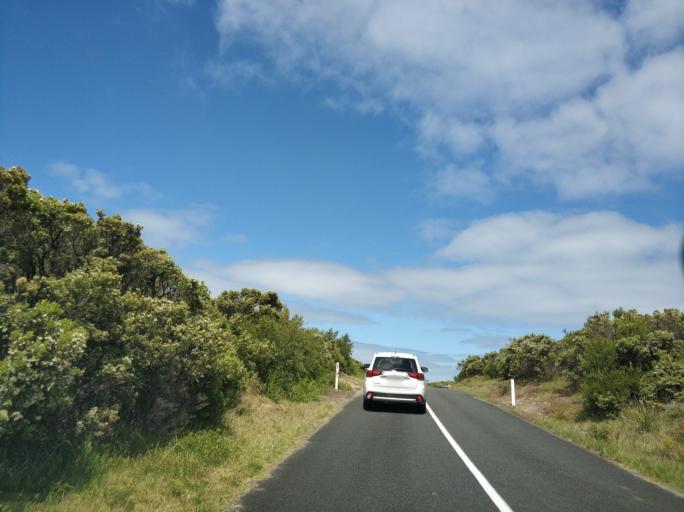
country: AU
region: Victoria
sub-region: Colac-Otway
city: Apollo Bay
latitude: -38.8521
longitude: 143.5246
